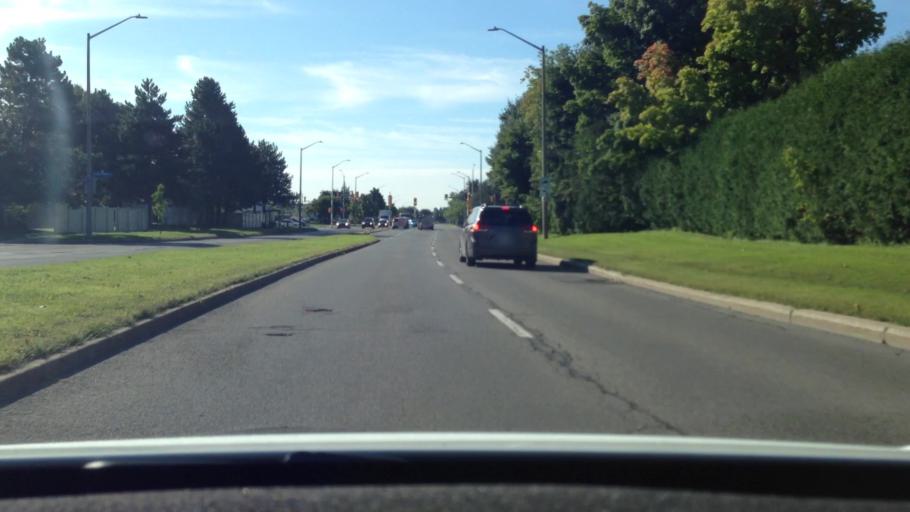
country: CA
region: Quebec
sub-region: Outaouais
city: Gatineau
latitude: 45.4635
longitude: -75.5272
